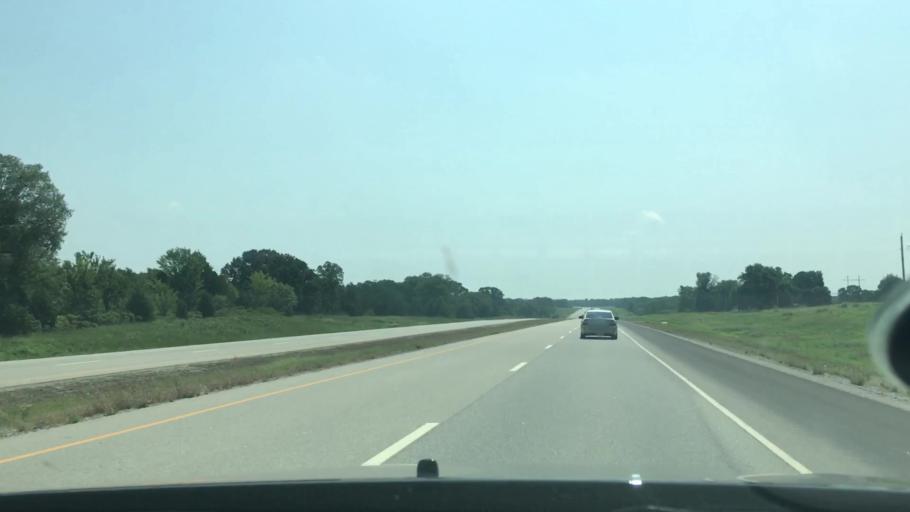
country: US
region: Oklahoma
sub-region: Atoka County
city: Atoka
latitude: 34.3295
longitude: -96.0487
